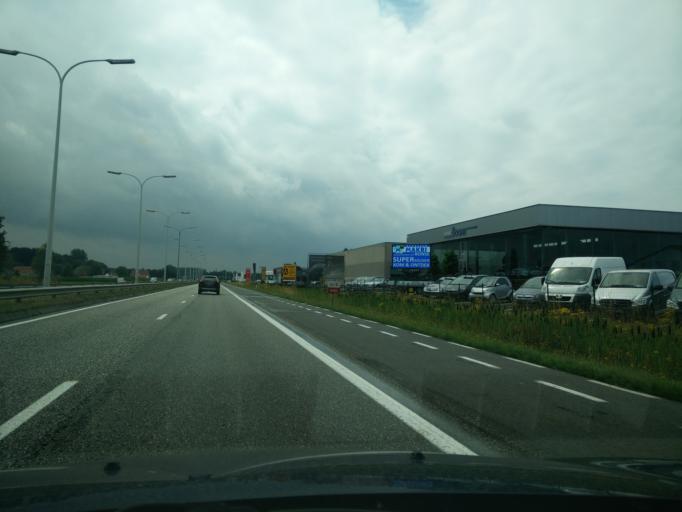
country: BE
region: Flanders
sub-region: Provincie Oost-Vlaanderen
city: De Pinte
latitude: 50.9734
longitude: 3.6604
